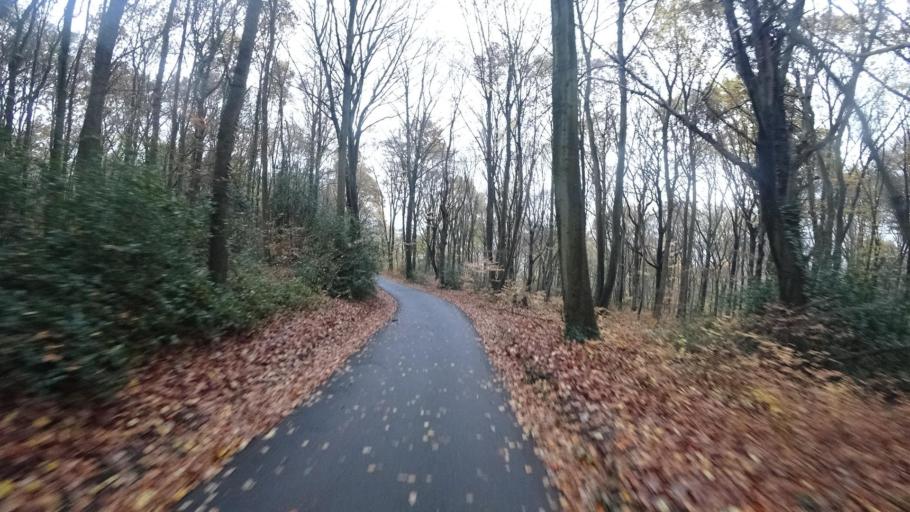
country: DE
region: Rheinland-Pfalz
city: Bad Neuenahr-Ahrweiler
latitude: 50.5356
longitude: 7.1213
